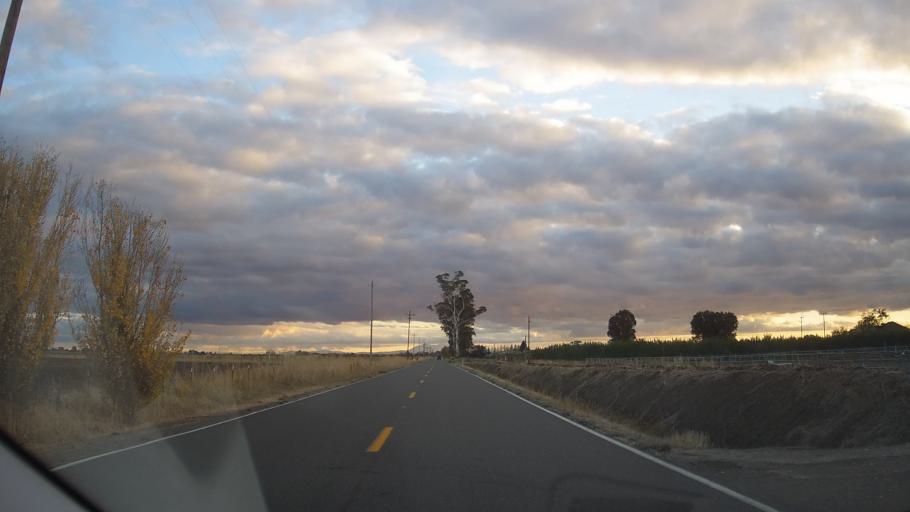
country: US
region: California
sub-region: Solano County
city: Hartley
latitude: 38.3825
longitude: -121.9059
